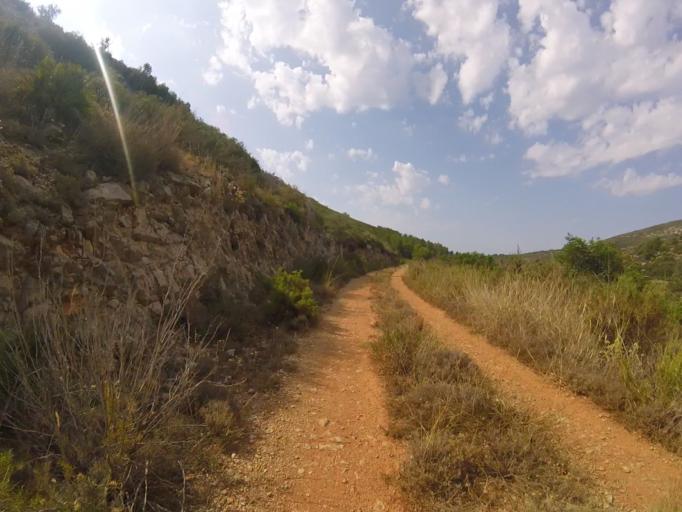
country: ES
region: Valencia
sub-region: Provincia de Castello
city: Alcala de Xivert
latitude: 40.3537
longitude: 0.2004
